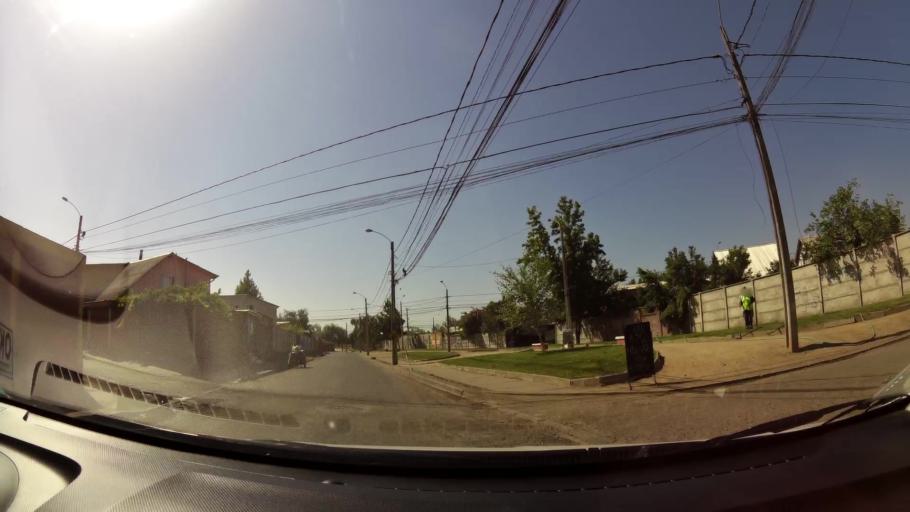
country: CL
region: Maule
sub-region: Provincia de Talca
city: Talca
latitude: -35.4113
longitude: -71.6392
